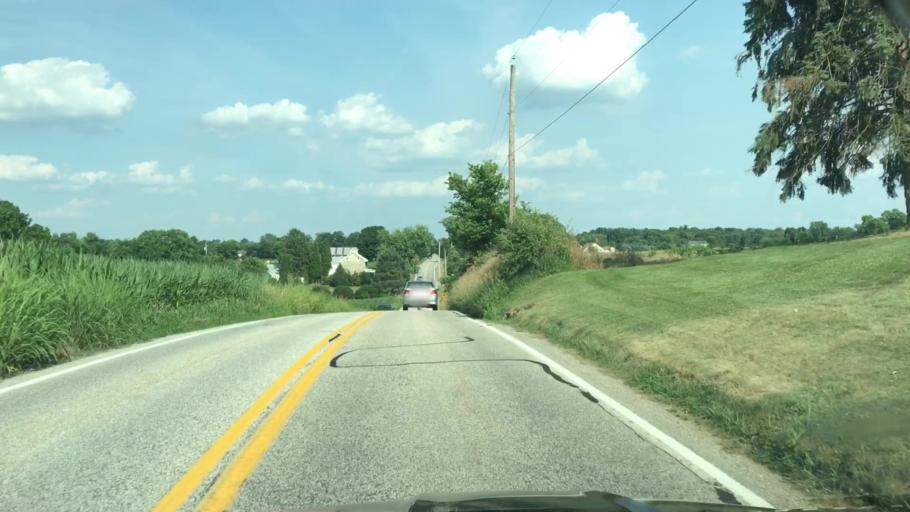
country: US
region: Pennsylvania
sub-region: Cumberland County
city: Boiling Springs
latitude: 40.1798
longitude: -77.0890
